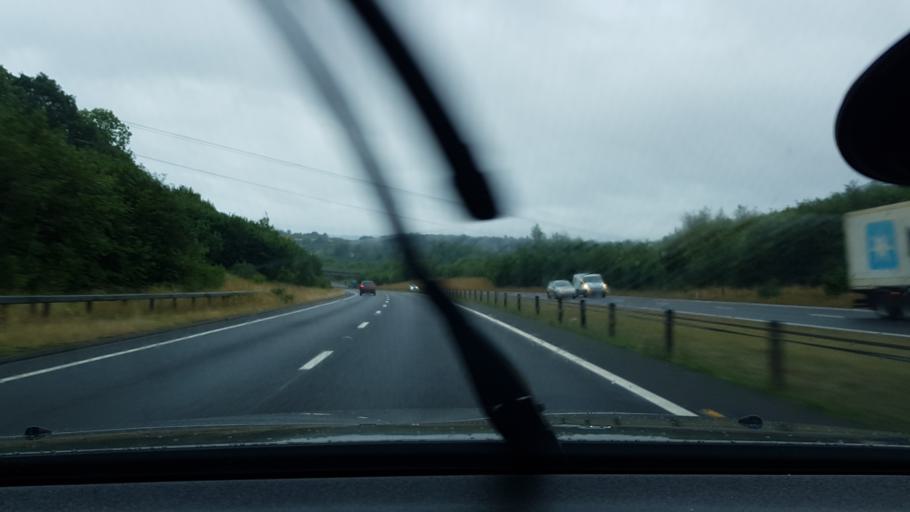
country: GB
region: England
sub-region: West Berkshire
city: Winterbourne
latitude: 51.4244
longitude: -1.3425
